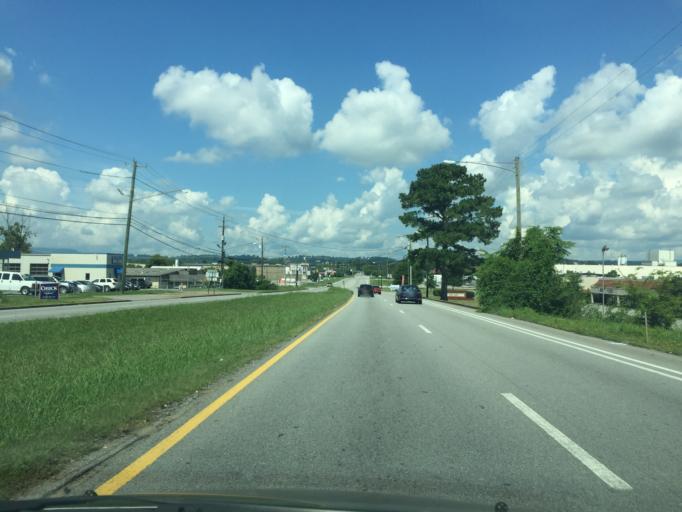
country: US
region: Tennessee
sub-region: Hamilton County
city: East Chattanooga
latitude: 35.0544
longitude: -85.1920
